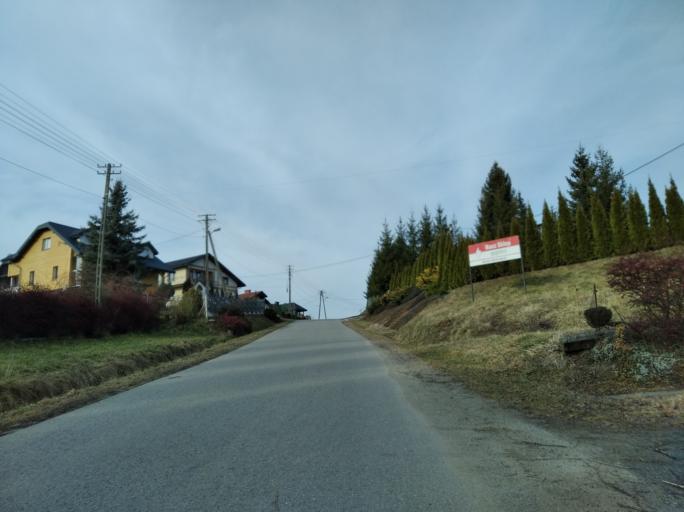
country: PL
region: Subcarpathian Voivodeship
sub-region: Powiat brzozowski
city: Turze Pole
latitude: 49.6690
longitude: 22.0033
